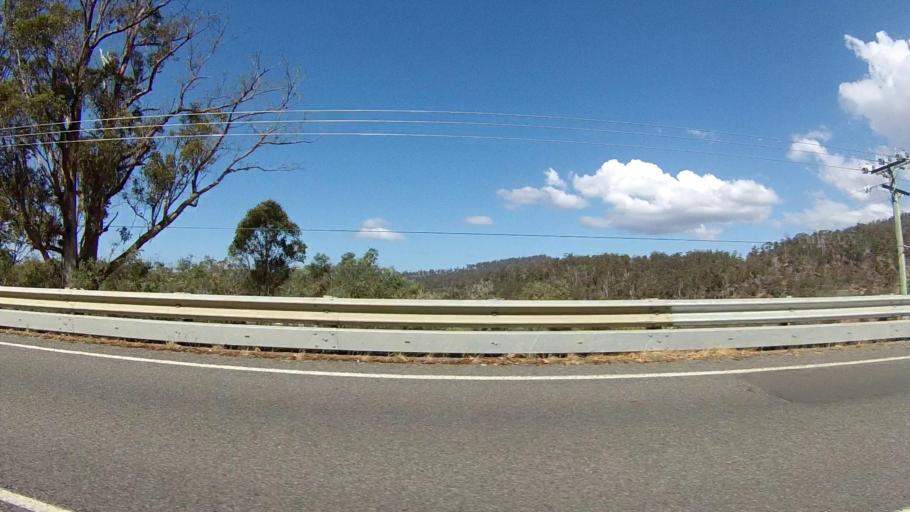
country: AU
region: Tasmania
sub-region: Sorell
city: Sorell
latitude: -42.6109
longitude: 147.6686
